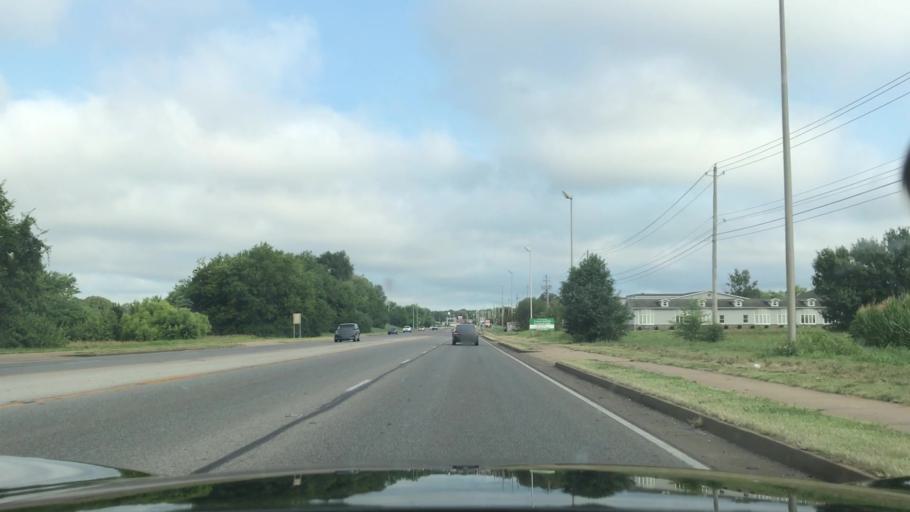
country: US
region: Kentucky
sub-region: Warren County
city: Bowling Green
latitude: 36.9550
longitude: -86.4452
